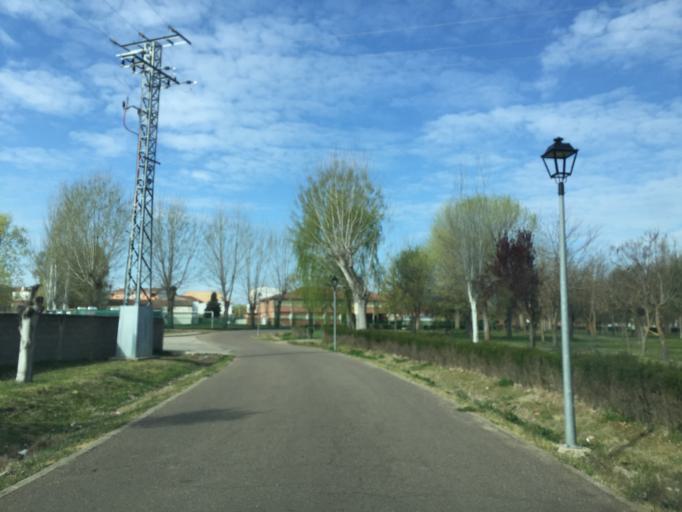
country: ES
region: Castille and Leon
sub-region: Provincia de Salamanca
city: Ciudad Rodrigo
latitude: 40.5918
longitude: -6.5345
